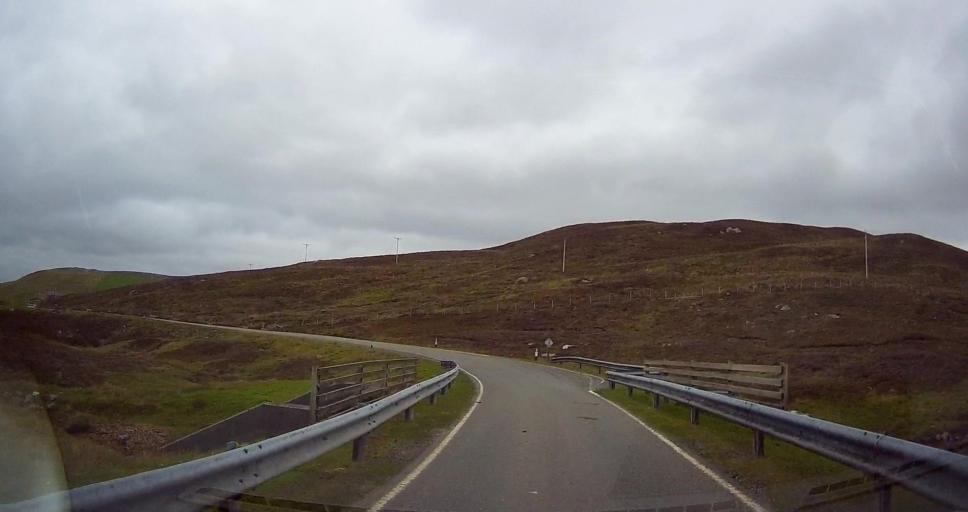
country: GB
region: Scotland
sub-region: Shetland Islands
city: Lerwick
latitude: 60.3299
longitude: -1.3364
